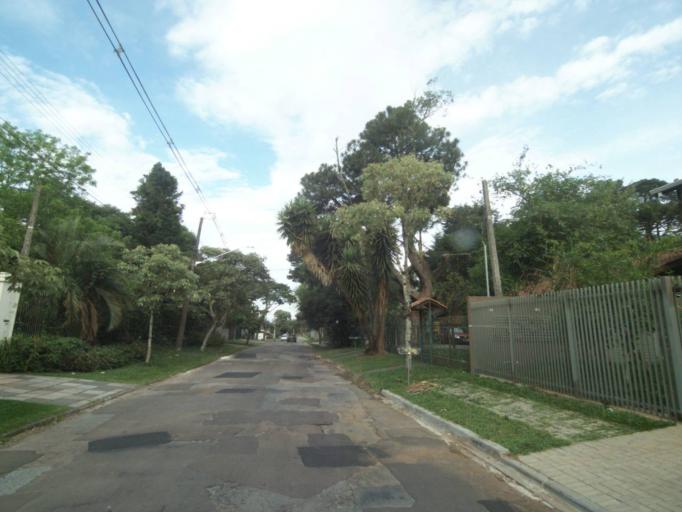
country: BR
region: Parana
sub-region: Curitiba
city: Curitiba
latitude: -25.4316
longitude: -49.2389
